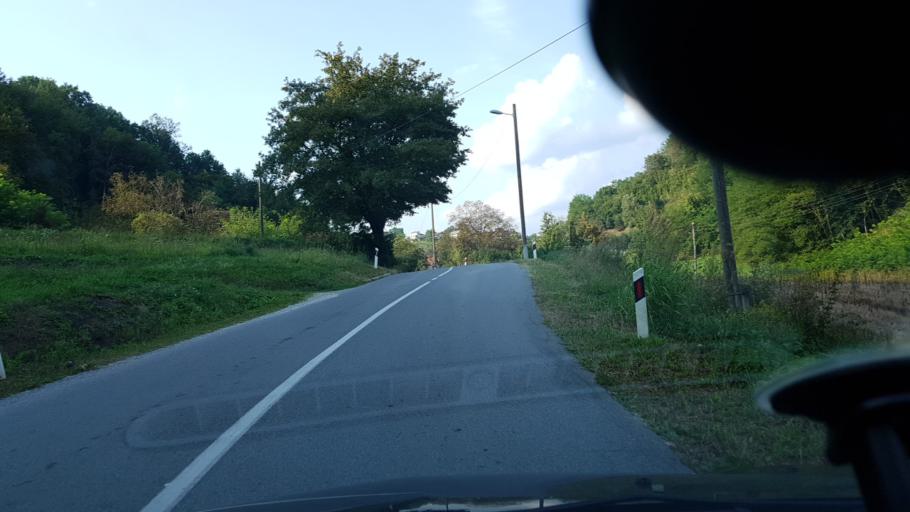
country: SI
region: Bistrica ob Sotli
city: Bistrica ob Sotli
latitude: 46.0550
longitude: 15.7708
